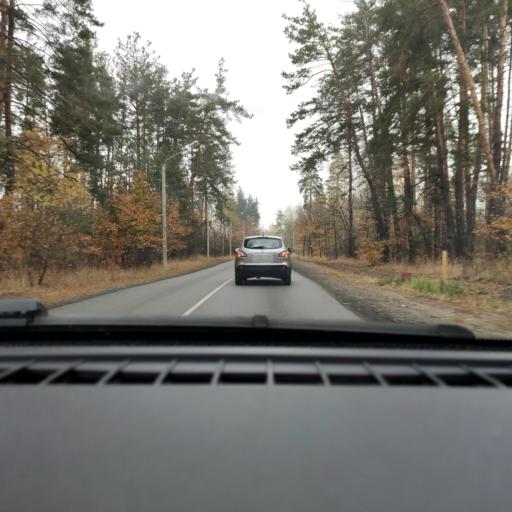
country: RU
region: Voronezj
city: Somovo
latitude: 51.7134
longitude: 39.3262
